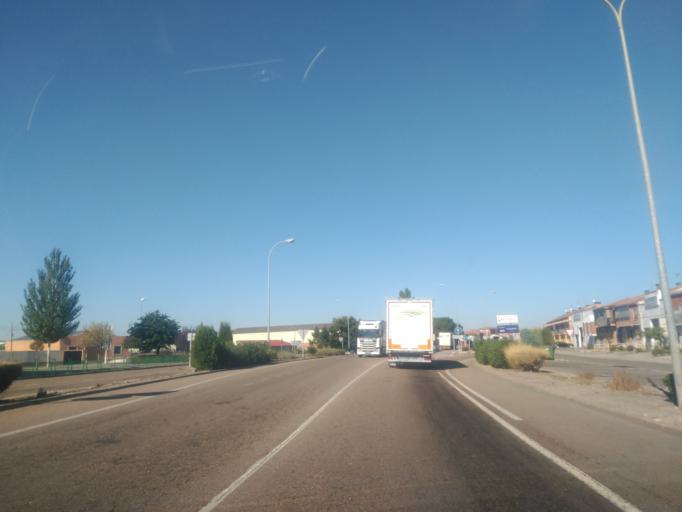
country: ES
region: Castille and Leon
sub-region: Provincia de Valladolid
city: Penafiel
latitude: 41.5989
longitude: -4.1282
